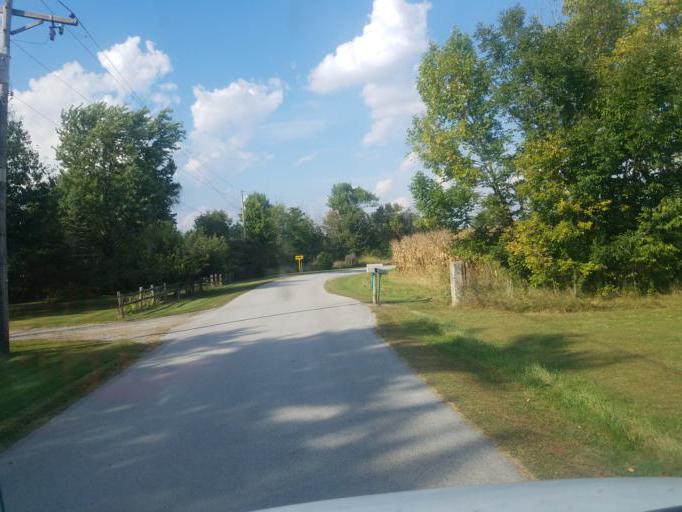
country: US
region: Ohio
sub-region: Hancock County
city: Arlington
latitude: 40.8796
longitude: -83.5709
